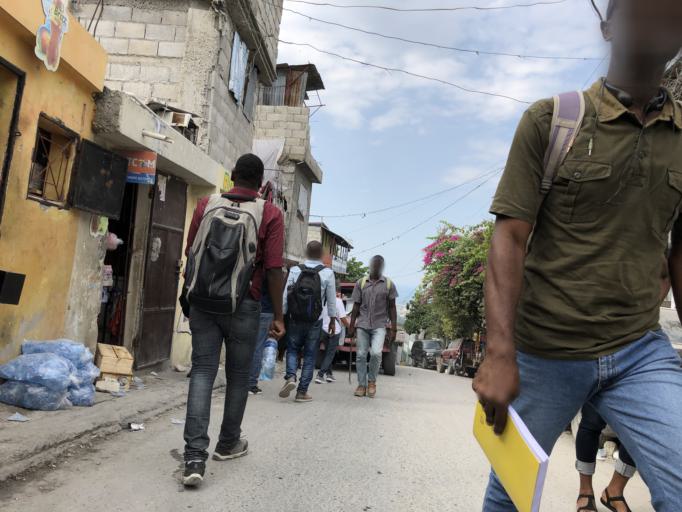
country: HT
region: Ouest
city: Port-au-Prince
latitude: 18.5246
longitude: -72.3185
